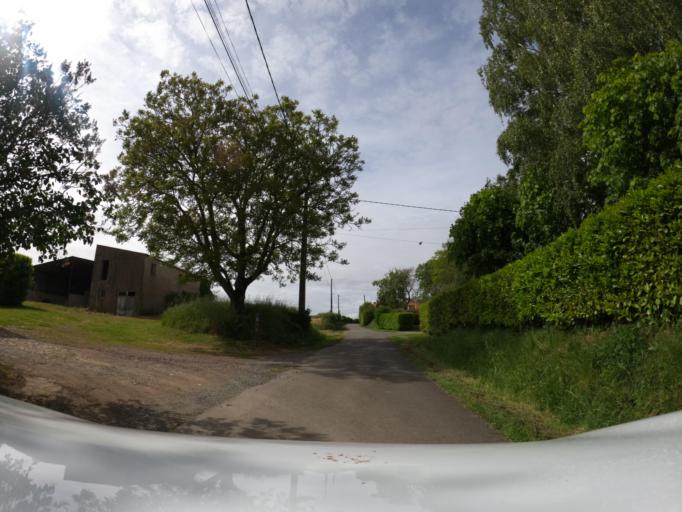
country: FR
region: Pays de la Loire
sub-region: Departement de la Vendee
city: Saint-Hilaire-des-Loges
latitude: 46.4912
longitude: -0.6613
